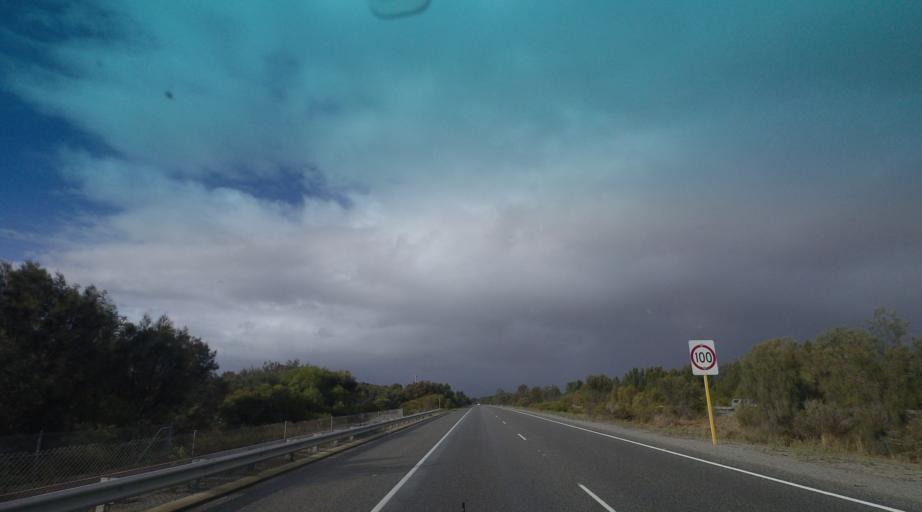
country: AU
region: Western Australia
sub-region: Serpentine-Jarrahdale
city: Oakford
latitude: -32.1926
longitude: 115.9625
